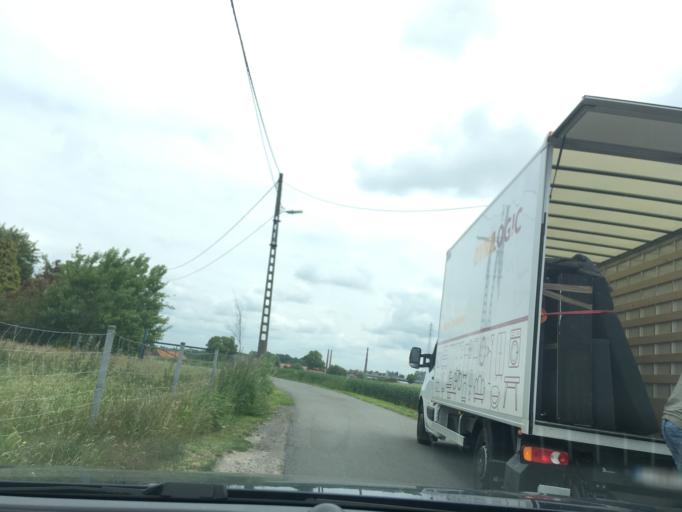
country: BE
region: Wallonia
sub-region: Province du Hainaut
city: Mouscron
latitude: 50.7642
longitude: 3.2063
